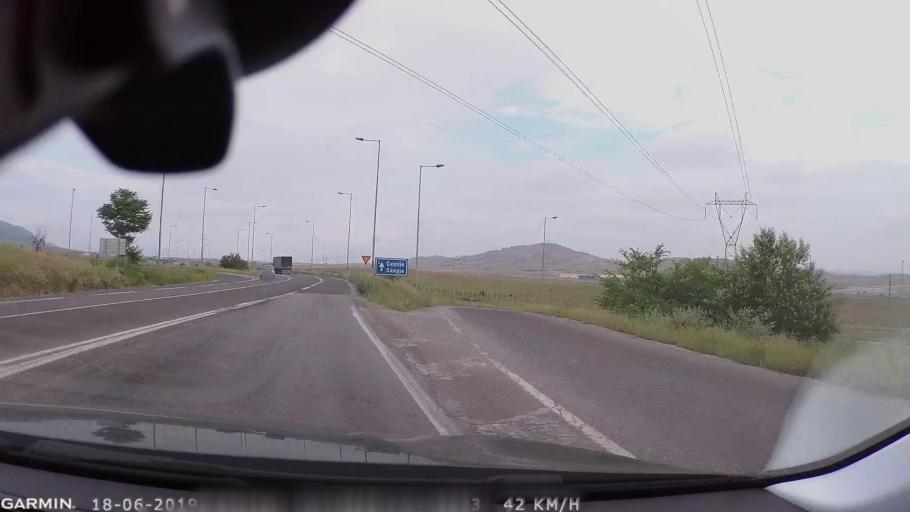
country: MK
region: Stip
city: Shtip
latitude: 41.7639
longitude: 22.1600
